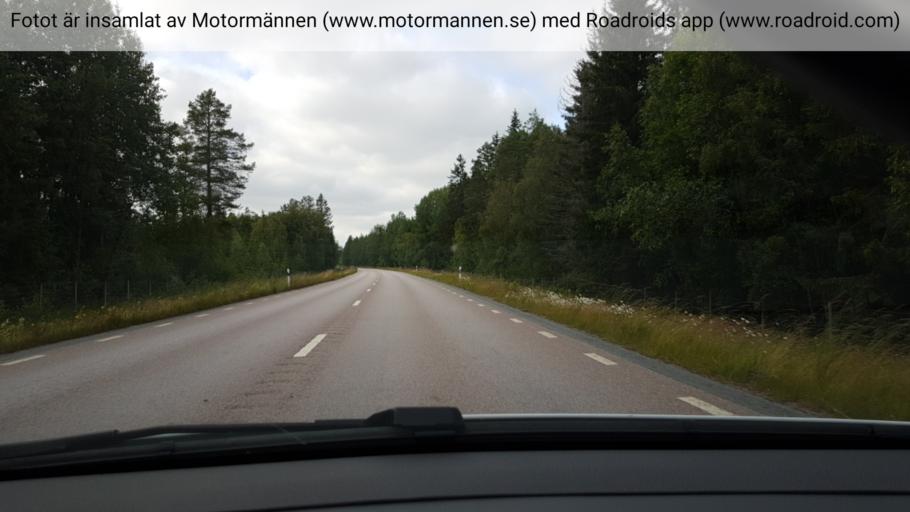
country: SE
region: Uppsala
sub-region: Osthammars Kommun
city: Osterbybruk
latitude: 60.4114
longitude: 17.8669
